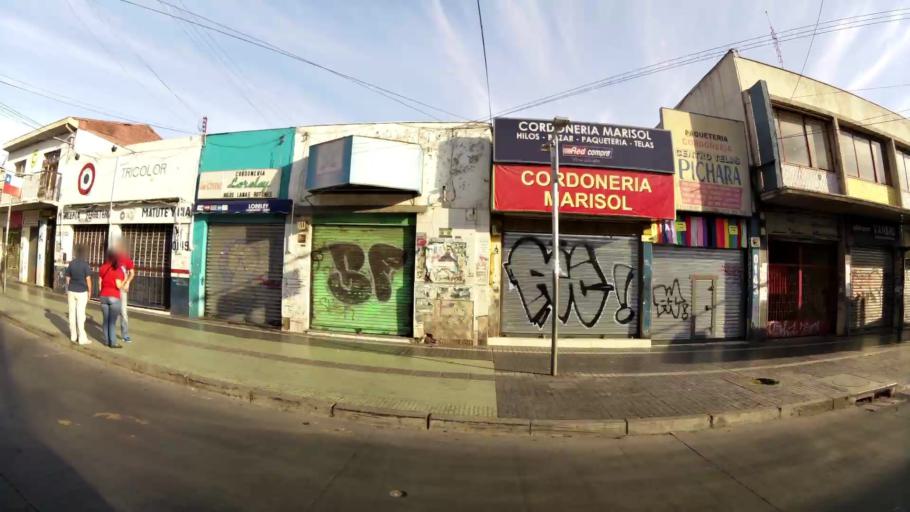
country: CL
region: Santiago Metropolitan
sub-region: Provincia de Cordillera
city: Puente Alto
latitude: -33.6091
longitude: -70.5743
